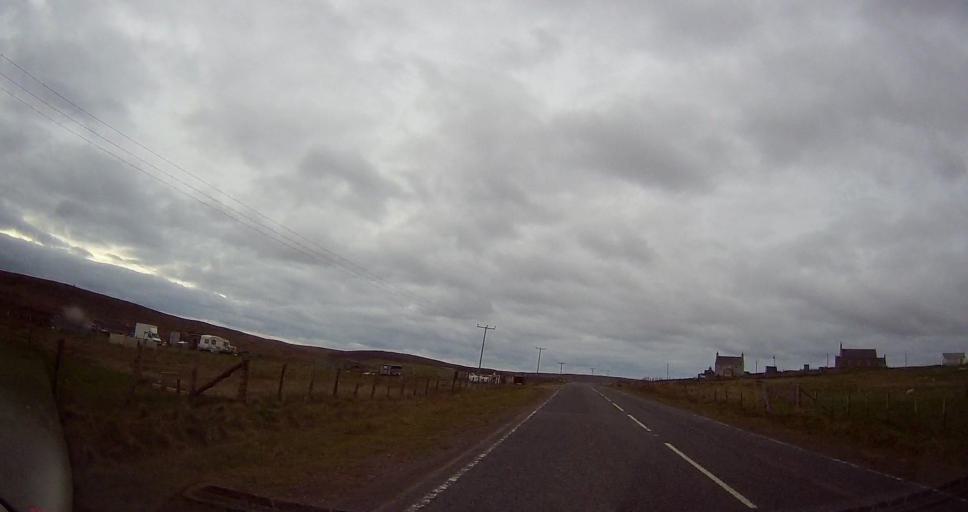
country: GB
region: Scotland
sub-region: Shetland Islands
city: Shetland
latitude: 60.6641
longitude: -1.0549
